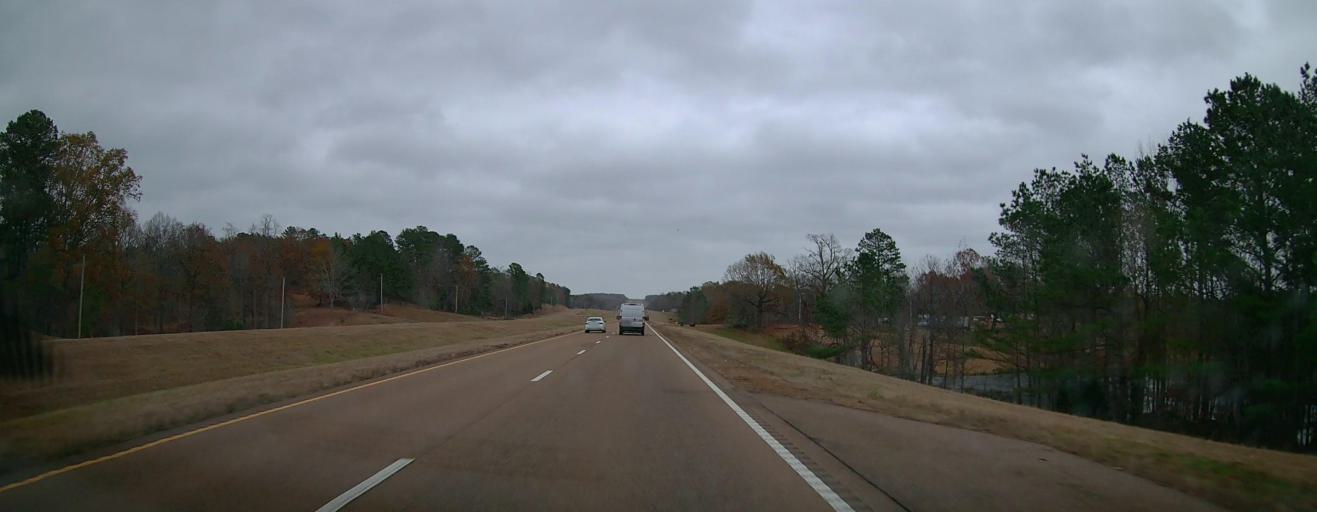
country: US
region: Mississippi
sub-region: Benton County
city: Ashland
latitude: 34.9506
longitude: -89.0772
